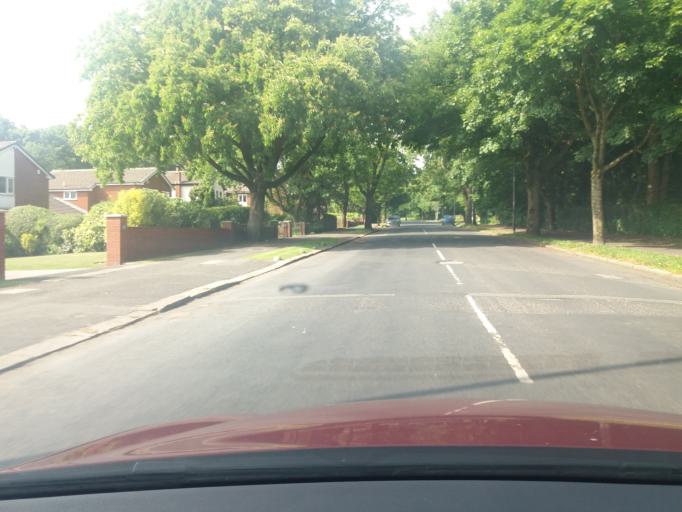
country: GB
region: England
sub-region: Borough of Bolton
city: Horwich
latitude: 53.6060
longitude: -2.5515
